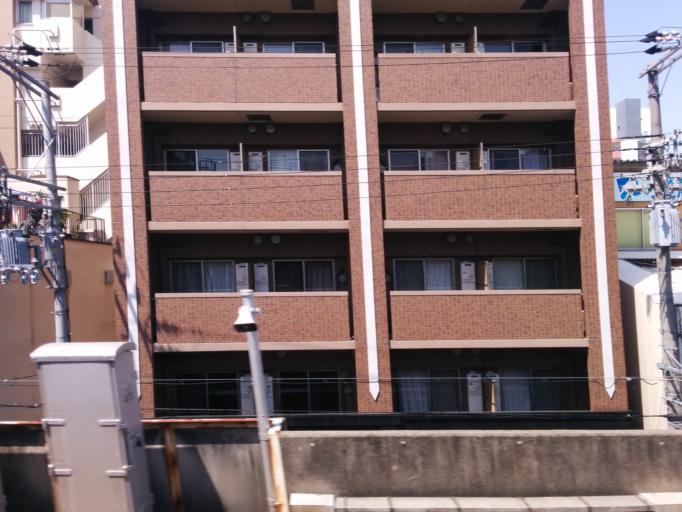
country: JP
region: Osaka
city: Osaka-shi
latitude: 34.7167
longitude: 135.5122
